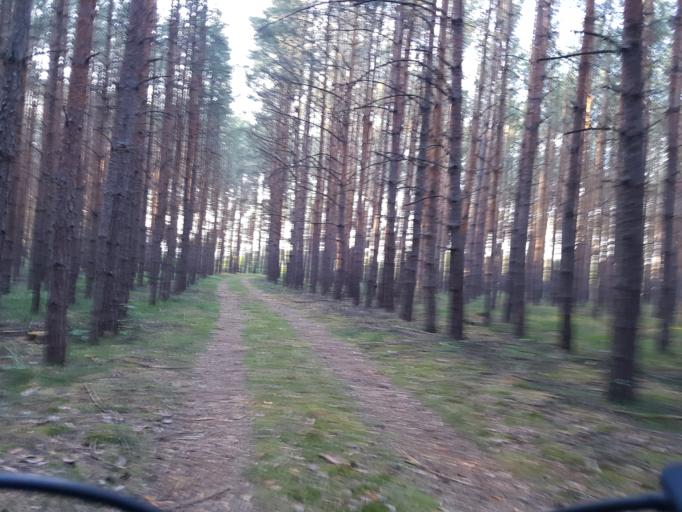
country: DE
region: Brandenburg
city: Schilda
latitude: 51.5879
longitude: 13.3511
